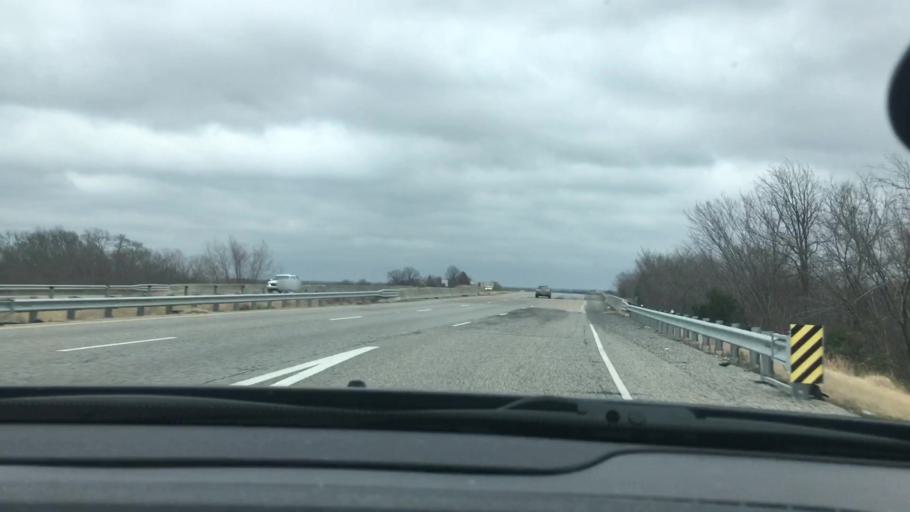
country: US
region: Oklahoma
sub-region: Bryan County
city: Durant
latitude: 34.0386
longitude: -96.3734
